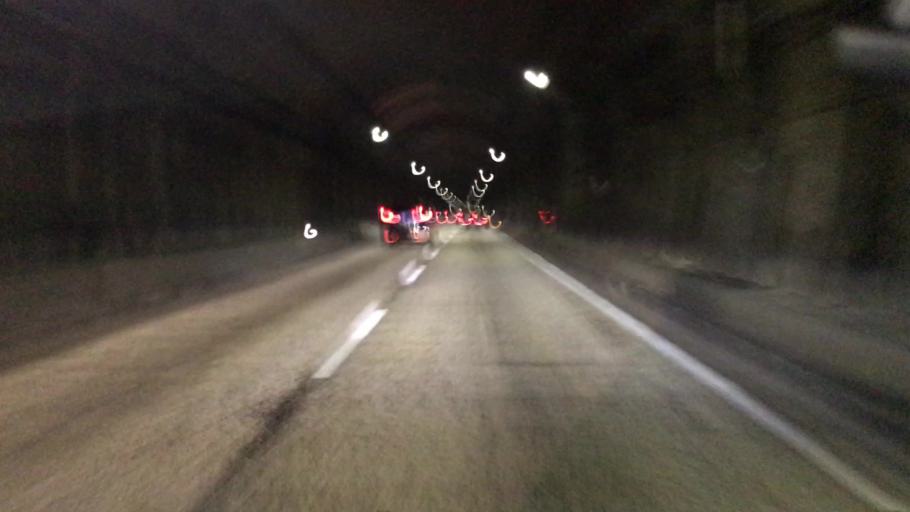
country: JP
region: Hyogo
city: Kobe
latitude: 34.7323
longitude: 135.1782
